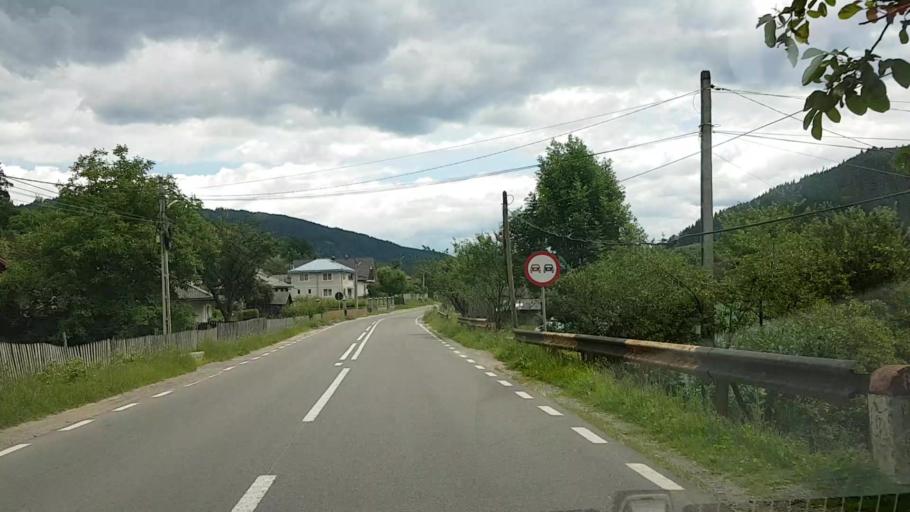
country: RO
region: Neamt
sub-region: Comuna Poiana Teiului
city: Poiana Teiului
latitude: 47.1188
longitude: 25.9160
